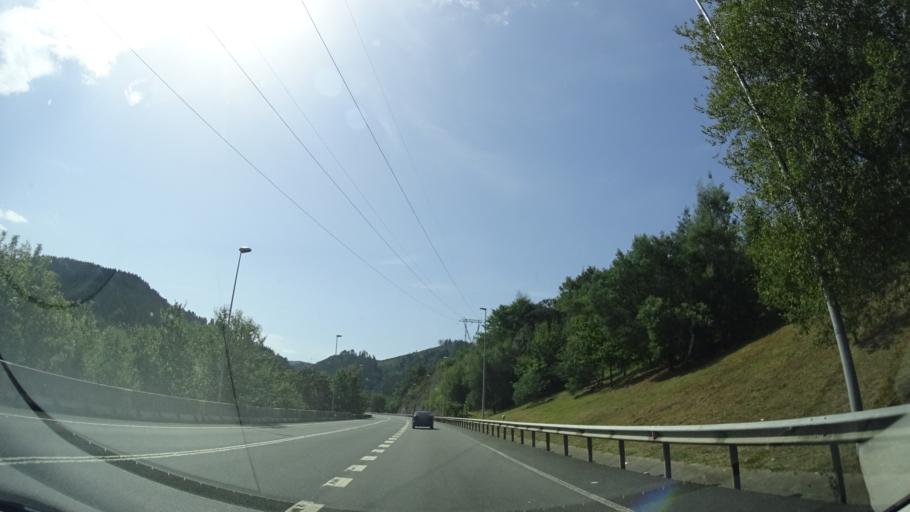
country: ES
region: Basque Country
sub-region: Bizkaia
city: Zeanuri
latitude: 43.0974
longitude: -2.7520
